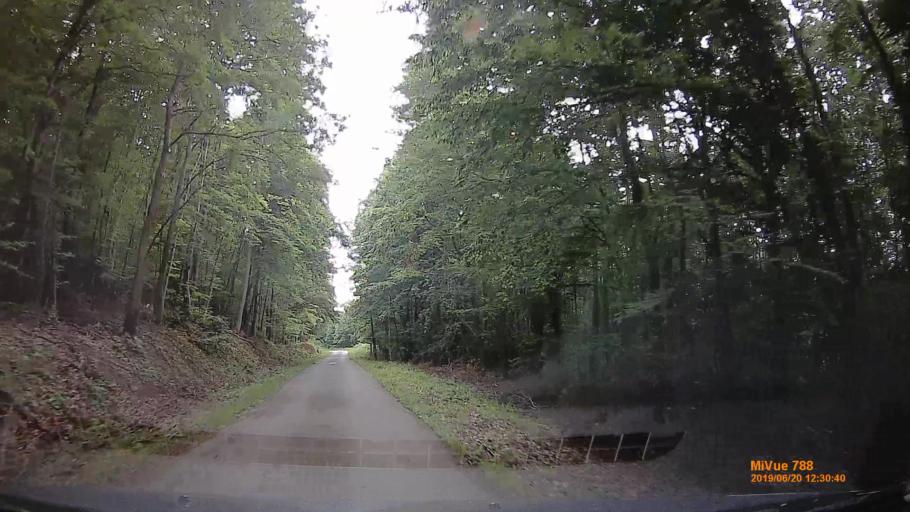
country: HU
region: Baranya
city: Hosszuheteny
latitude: 46.1996
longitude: 18.3587
